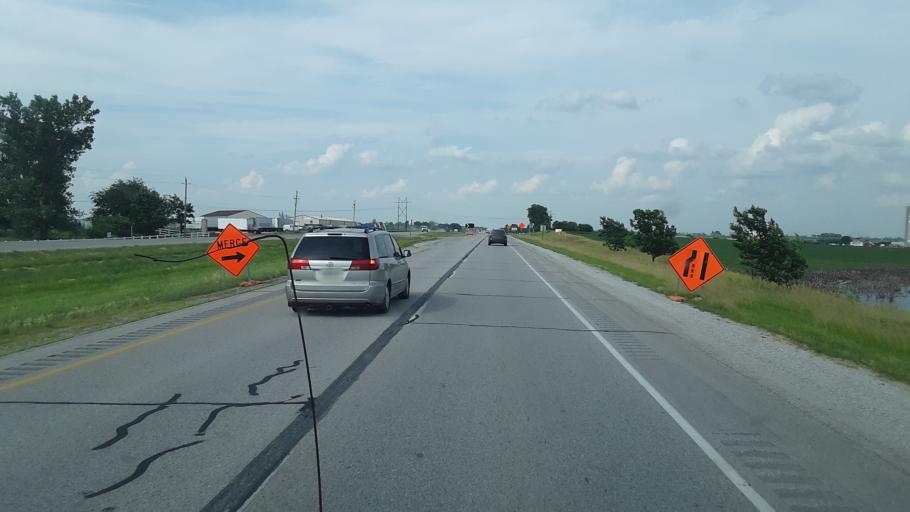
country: US
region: Iowa
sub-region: Polk County
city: Bondurant
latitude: 41.6752
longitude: -93.4777
